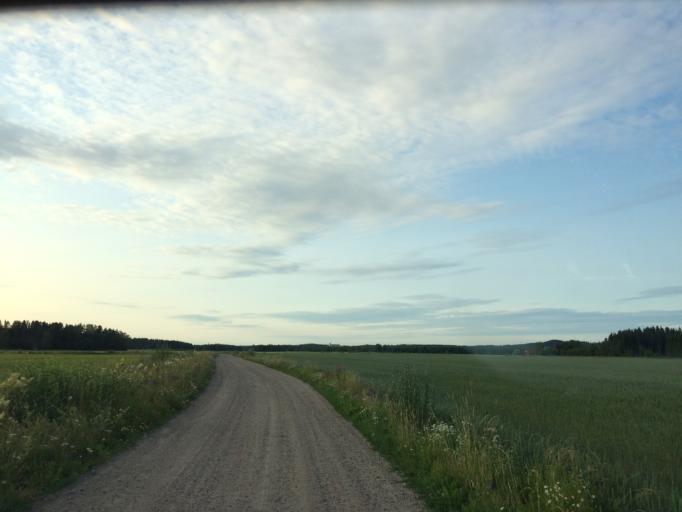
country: FI
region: Haeme
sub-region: Haemeenlinna
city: Janakkala
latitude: 60.8797
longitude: 24.6299
